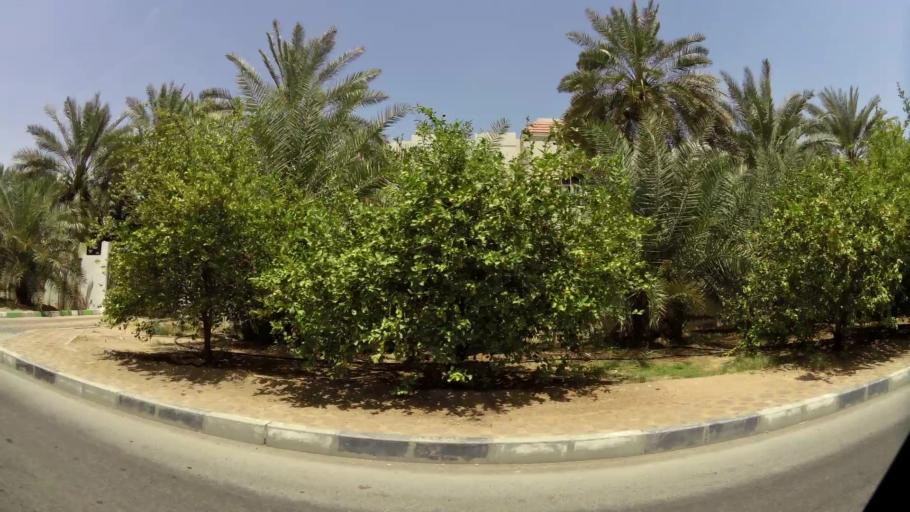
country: AE
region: Abu Dhabi
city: Al Ain
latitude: 24.2564
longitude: 55.7105
